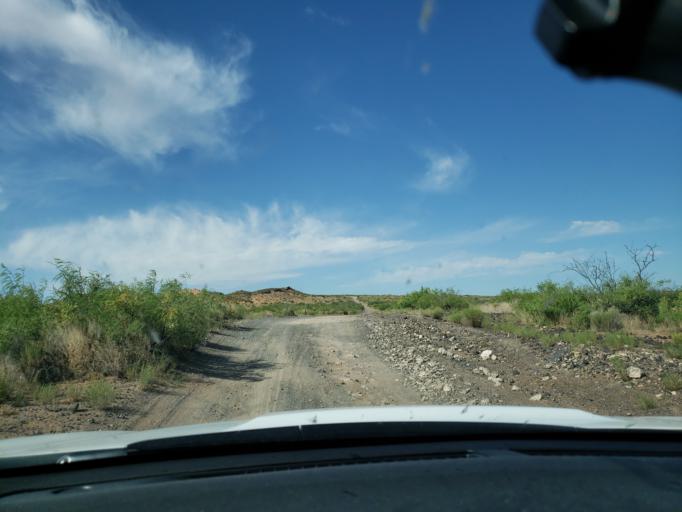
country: US
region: New Mexico
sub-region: Dona Ana County
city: San Miguel
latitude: 32.0829
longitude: -106.7902
